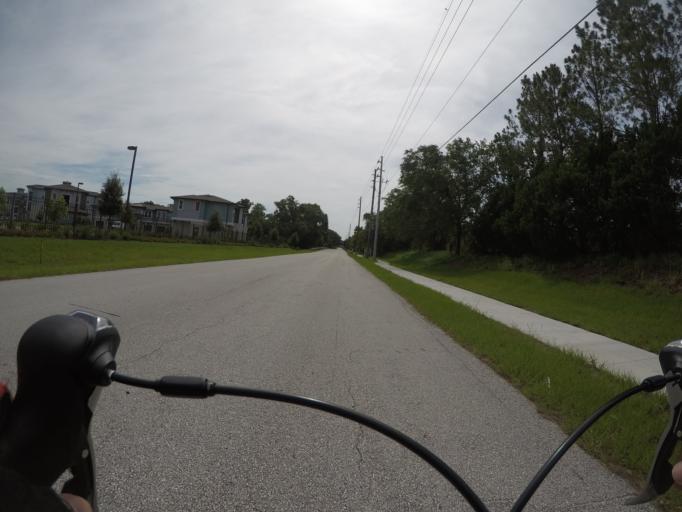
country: US
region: Florida
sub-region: Osceola County
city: Buenaventura Lakes
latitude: 28.3782
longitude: -81.2403
